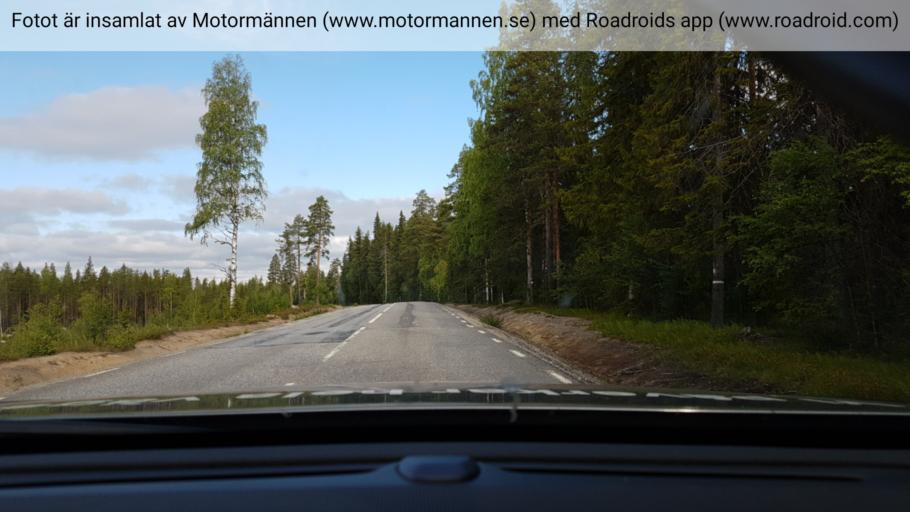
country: SE
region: Vaesterbotten
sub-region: Norsjo Kommun
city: Norsjoe
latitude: 64.6919
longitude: 19.1976
